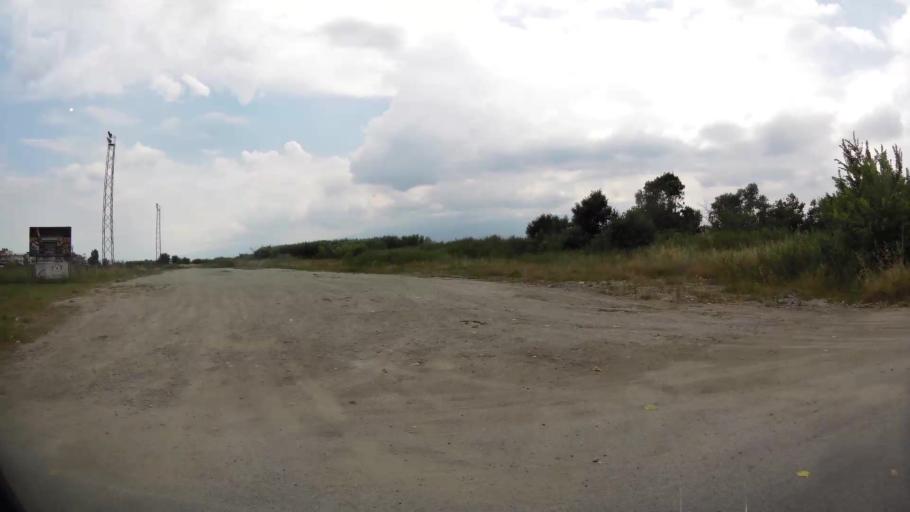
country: GR
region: Central Macedonia
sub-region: Nomos Pierias
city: Paralia
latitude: 40.2640
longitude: 22.5928
